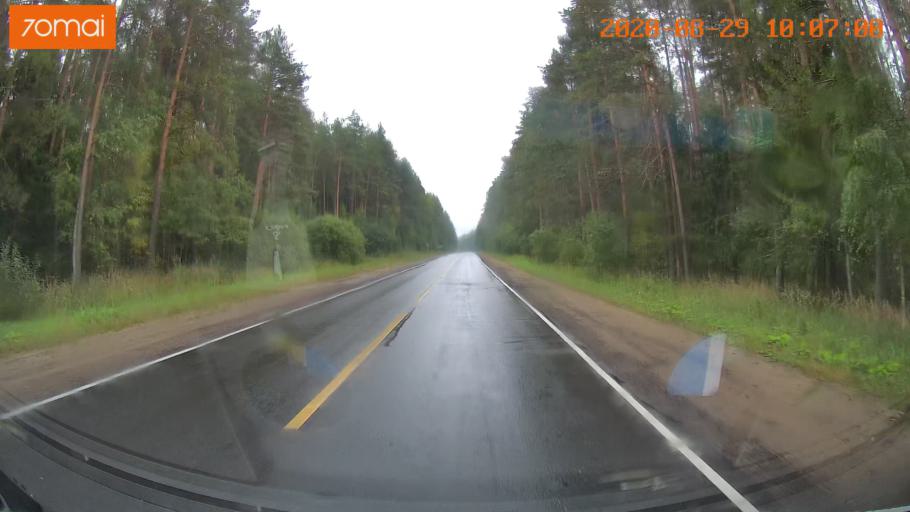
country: RU
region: Ivanovo
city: Kuznechikha
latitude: 57.3847
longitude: 42.5577
